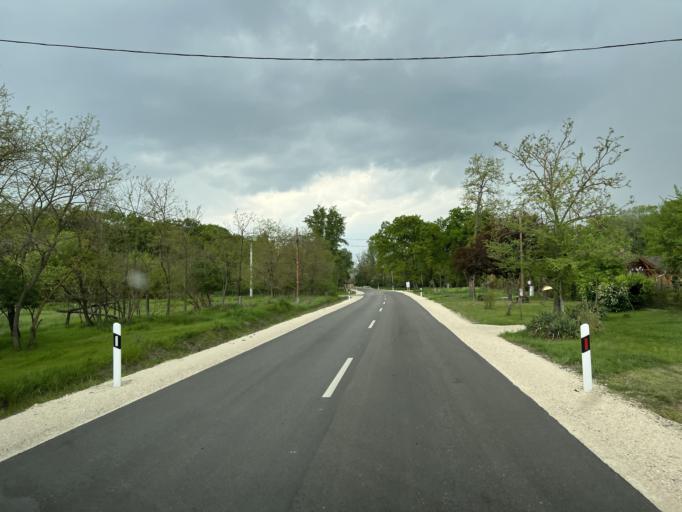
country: HU
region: Pest
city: Nagykoros
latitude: 47.0564
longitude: 19.7186
